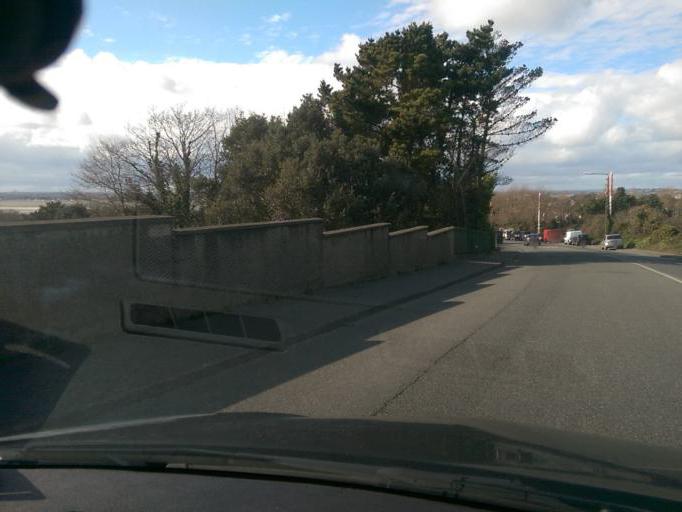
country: IE
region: Leinster
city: Sutton
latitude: 53.3787
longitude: -6.0915
